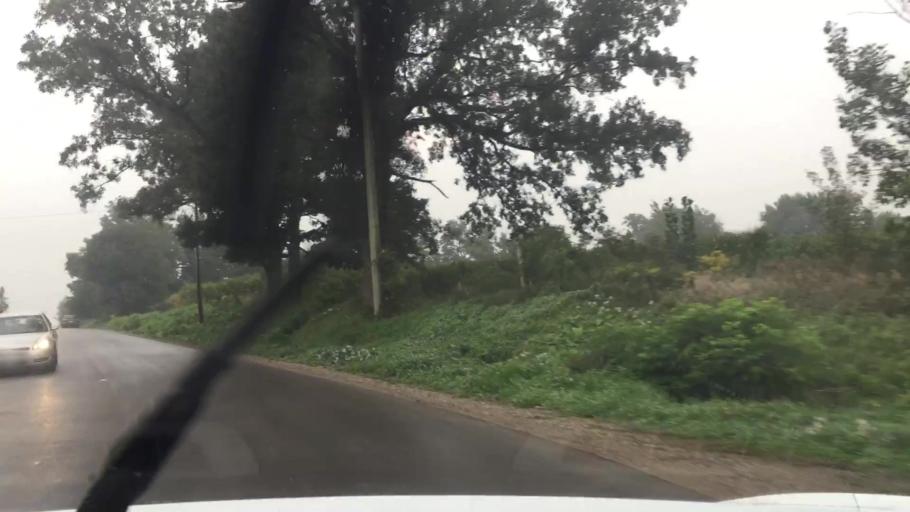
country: CA
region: Ontario
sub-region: Oxford County
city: Woodstock
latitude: 43.1058
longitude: -80.7307
